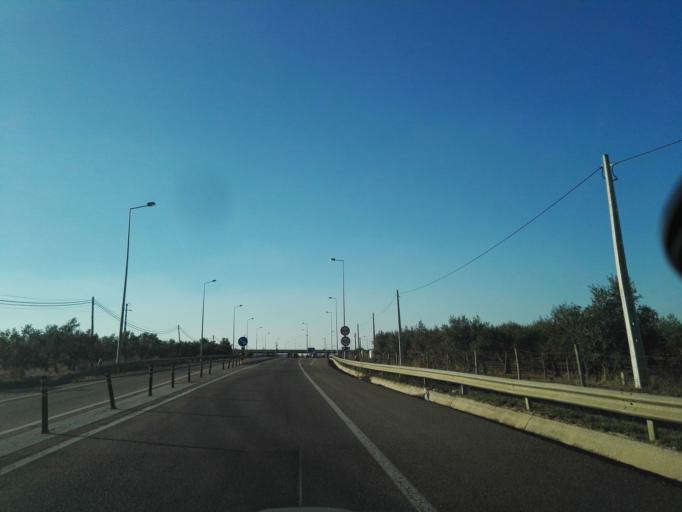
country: PT
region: Evora
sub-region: Borba
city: Borba
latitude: 38.8111
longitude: -7.4711
